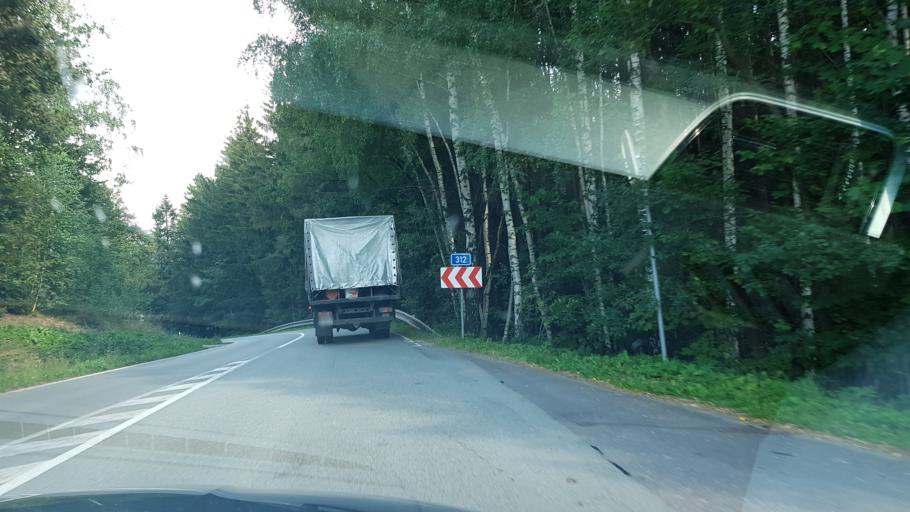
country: CZ
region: Pardubicky
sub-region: Okres Usti nad Orlici
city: Kunvald
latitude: 50.0887
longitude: 16.5518
